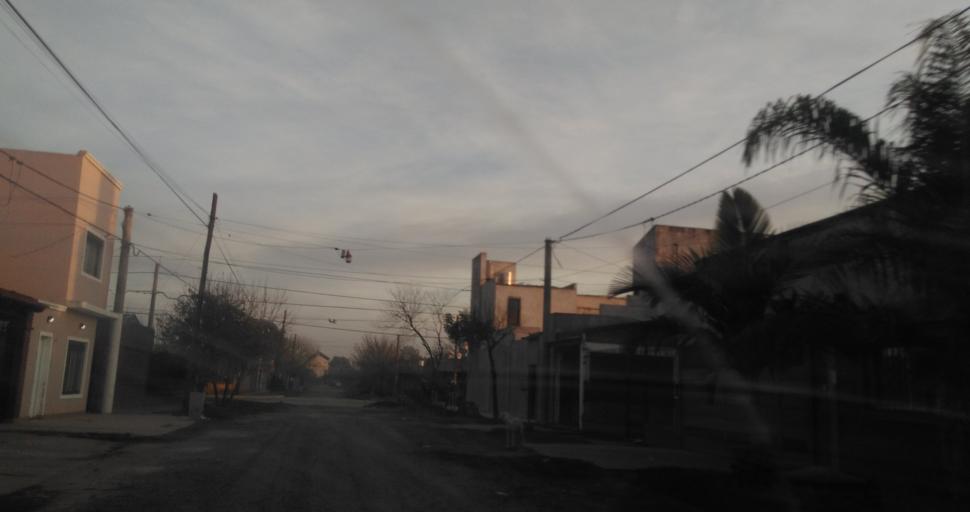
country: AR
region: Chaco
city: Resistencia
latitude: -27.4641
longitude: -59.0106
